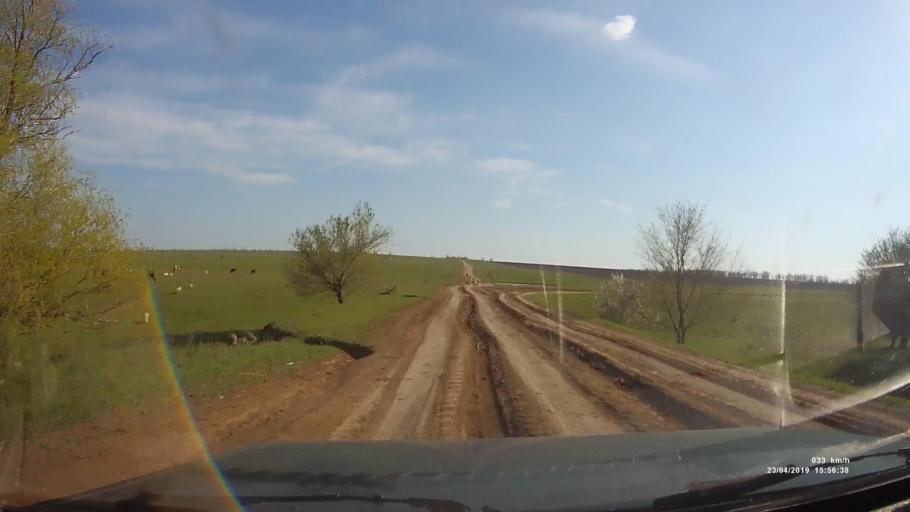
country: RU
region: Rostov
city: Remontnoye
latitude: 46.5360
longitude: 43.1110
